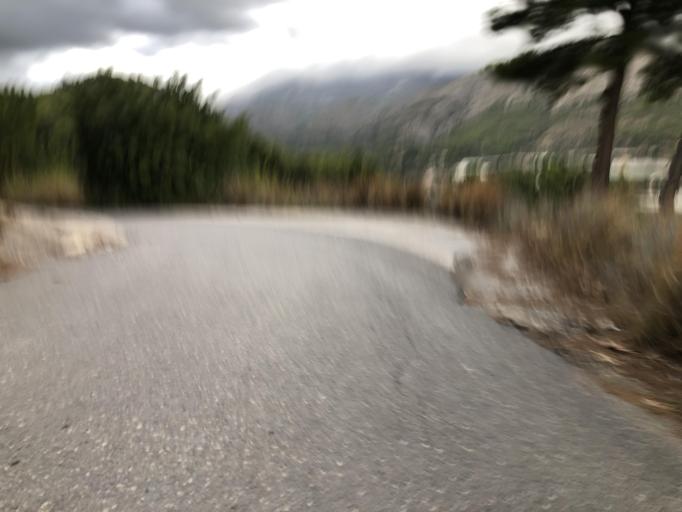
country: ES
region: Valencia
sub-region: Provincia de Alicante
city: Polop
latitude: 38.6376
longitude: -0.1330
